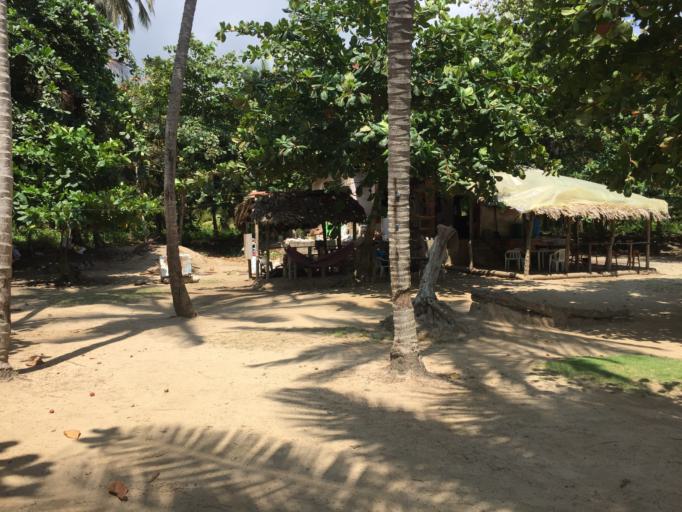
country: CO
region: Magdalena
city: Santa Marta
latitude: 11.3171
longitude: -73.9526
